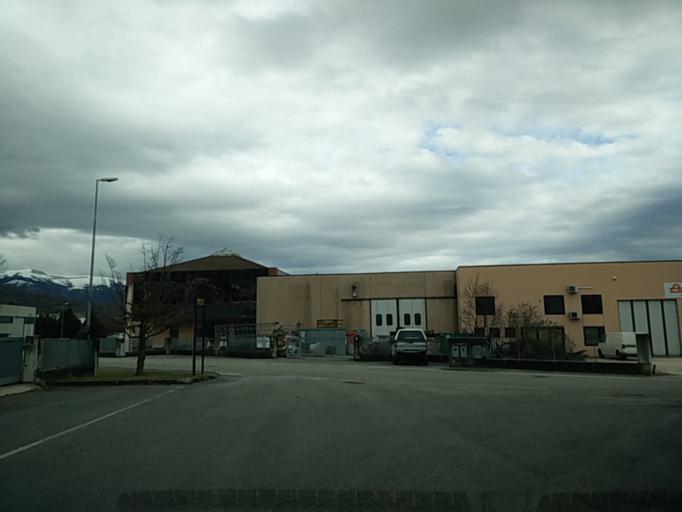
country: IT
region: Veneto
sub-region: Provincia di Treviso
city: Caniezza
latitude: 45.8541
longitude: 11.8940
